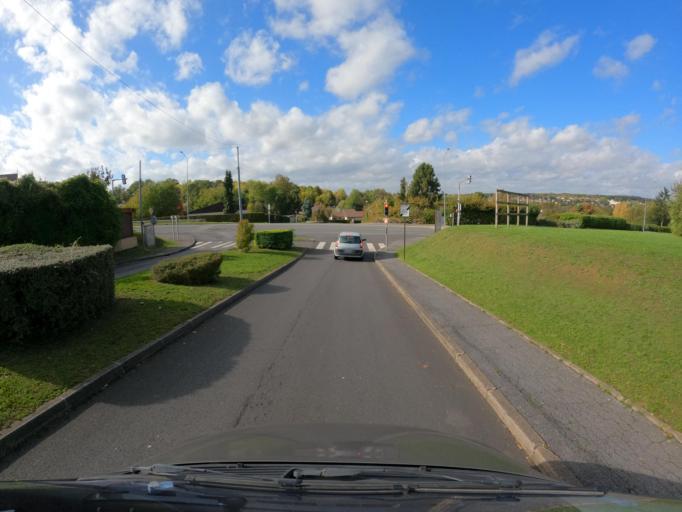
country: FR
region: Ile-de-France
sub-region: Departement de Seine-et-Marne
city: Esbly
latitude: 48.8943
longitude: 2.8099
